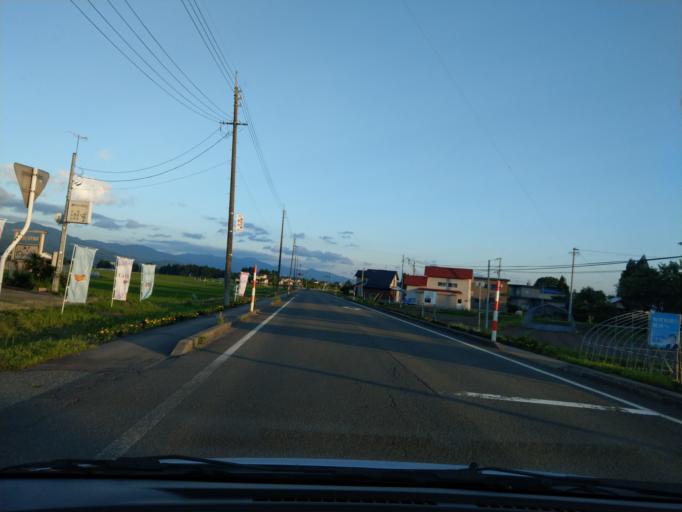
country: JP
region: Akita
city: Kakunodatemachi
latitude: 39.6412
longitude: 140.5717
